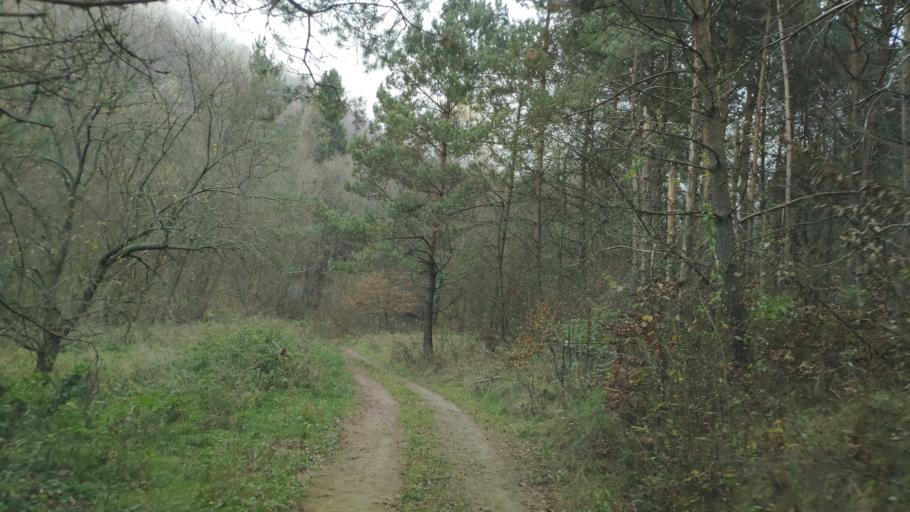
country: SK
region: Presovsky
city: Sabinov
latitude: 49.1428
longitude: 21.2157
